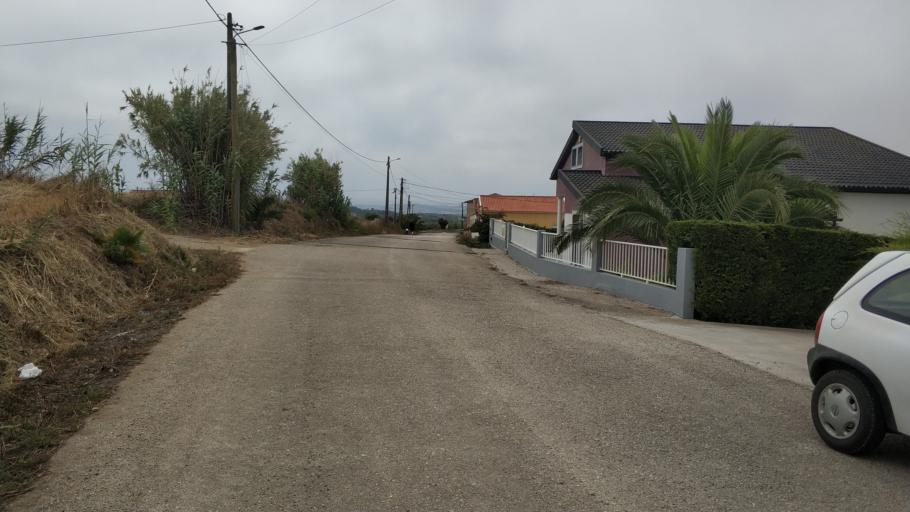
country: PT
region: Lisbon
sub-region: Lourinha
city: Lourinha
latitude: 39.2109
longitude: -9.3211
